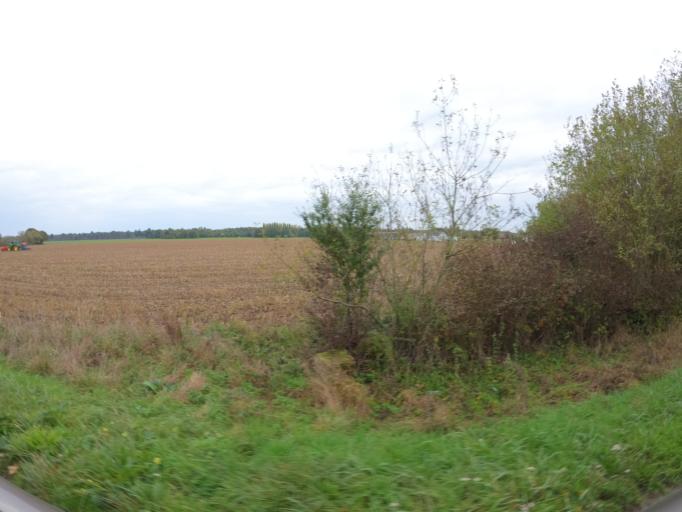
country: FR
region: Ile-de-France
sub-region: Departement de Seine-et-Marne
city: Villeneuve-le-Comte
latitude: 48.8205
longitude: 2.8321
